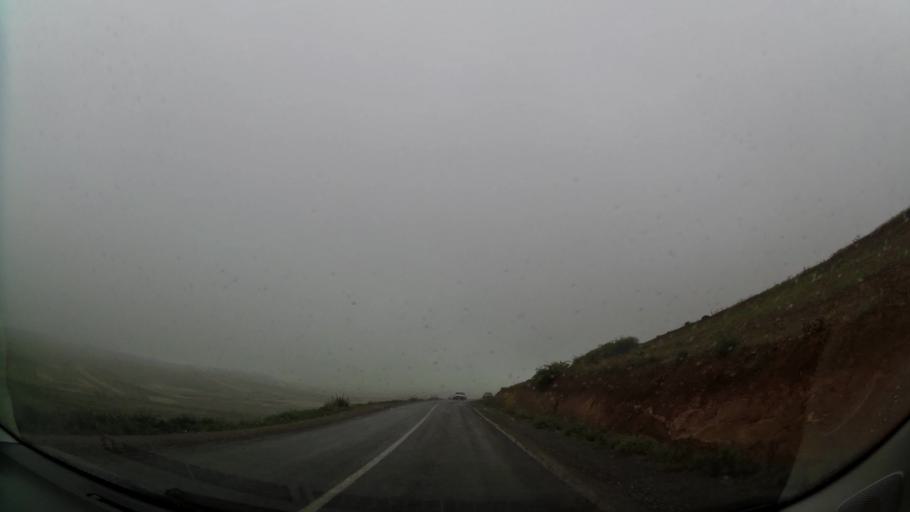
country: MA
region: Oriental
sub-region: Nador
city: Boudinar
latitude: 35.1379
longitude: -3.6031
